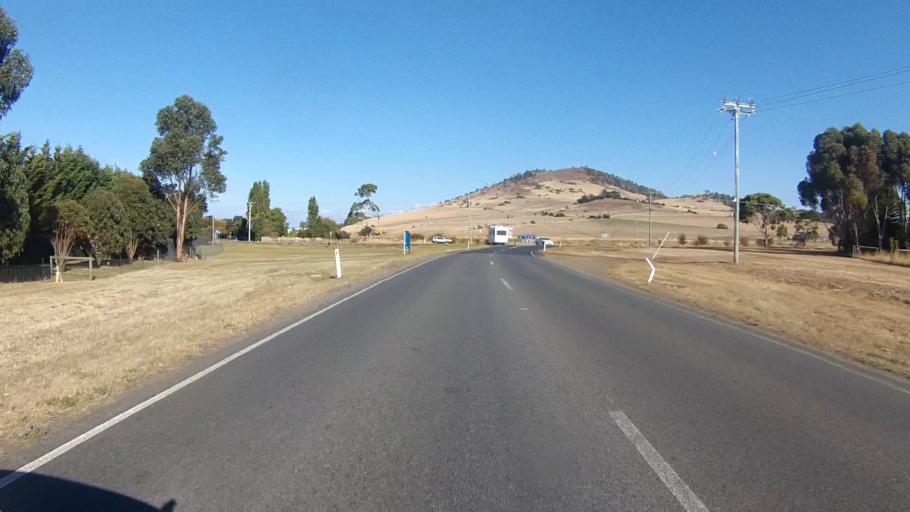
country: AU
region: Tasmania
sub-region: Clarence
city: Seven Mile Beach
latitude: -42.8601
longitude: 147.4931
